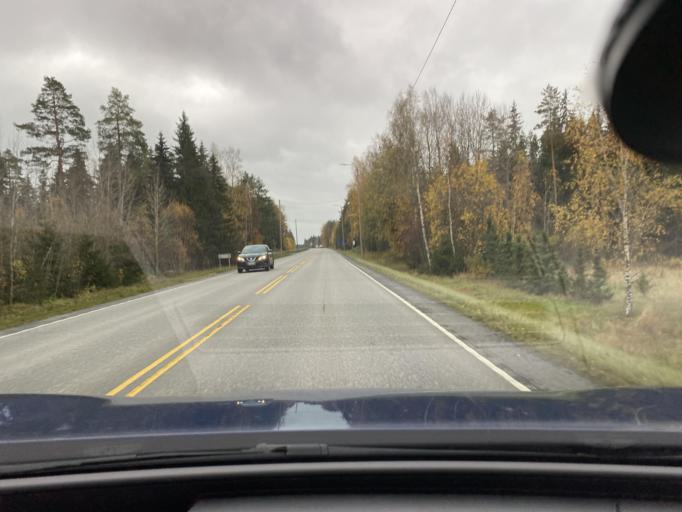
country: FI
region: Varsinais-Suomi
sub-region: Vakka-Suomi
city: Laitila
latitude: 60.9636
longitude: 21.5945
